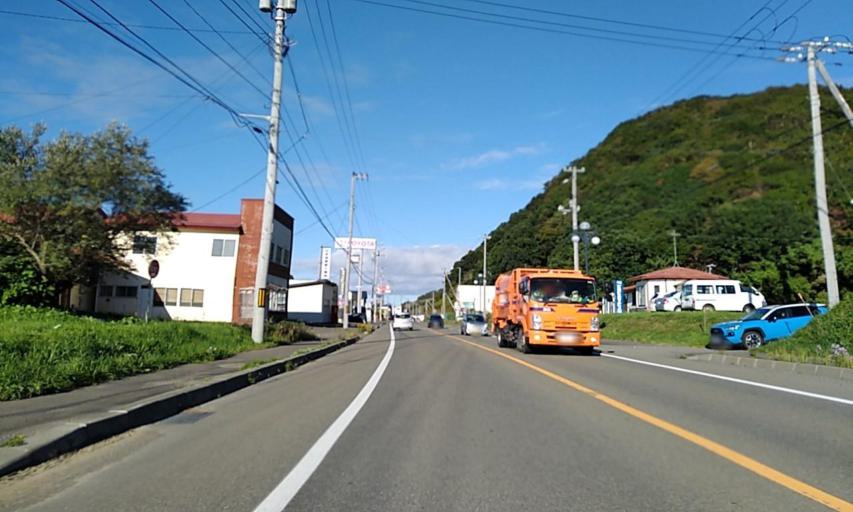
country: JP
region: Hokkaido
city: Shizunai-furukawacho
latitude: 42.1765
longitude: 142.7567
